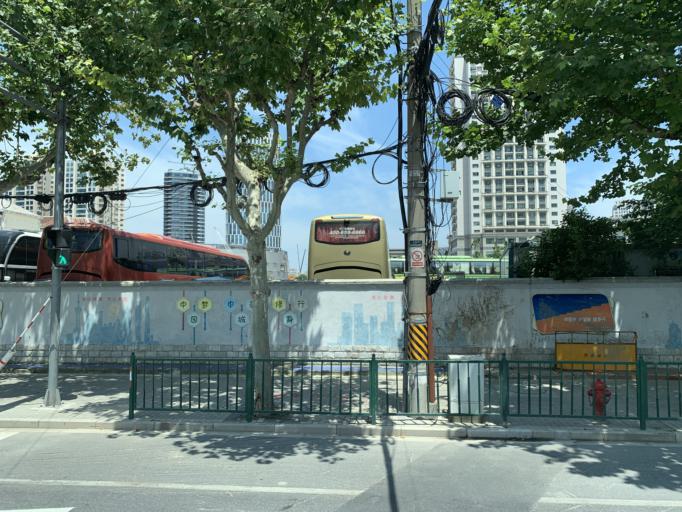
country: CN
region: Shanghai Shi
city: Pudong
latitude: 31.2442
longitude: 121.5373
